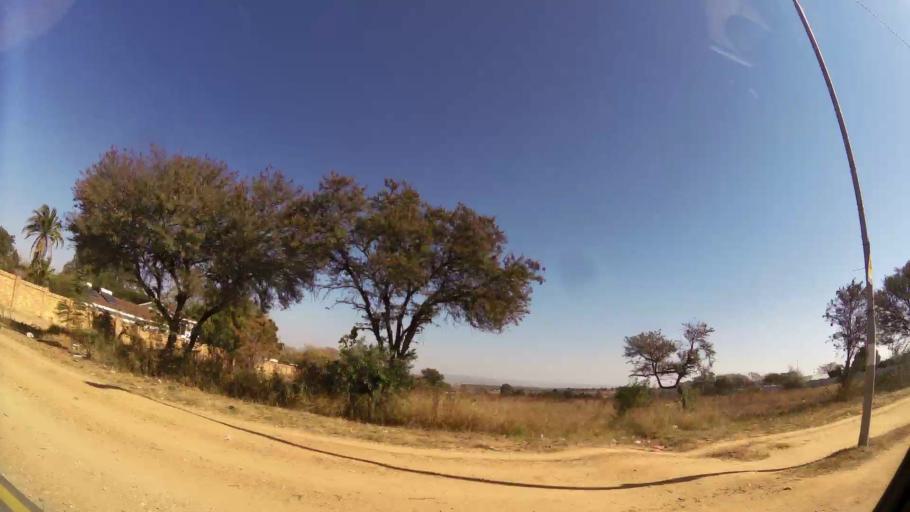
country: ZA
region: Gauteng
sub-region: City of Johannesburg Metropolitan Municipality
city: Midrand
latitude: -25.9435
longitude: 28.0968
